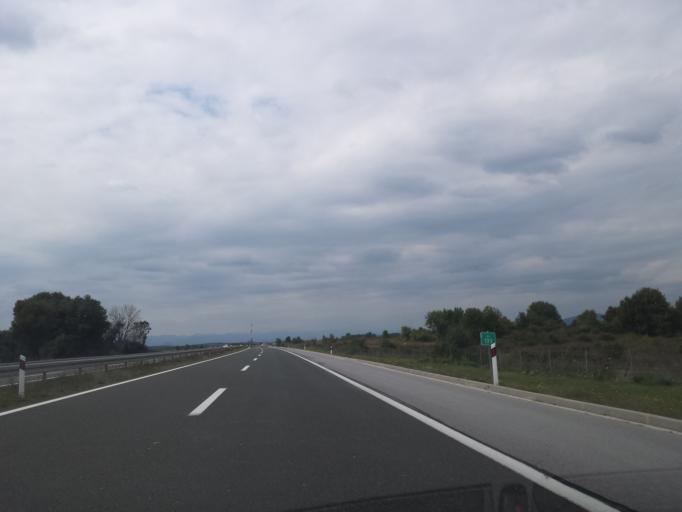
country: HR
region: Licko-Senjska
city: Gospic
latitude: 44.4759
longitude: 15.5779
